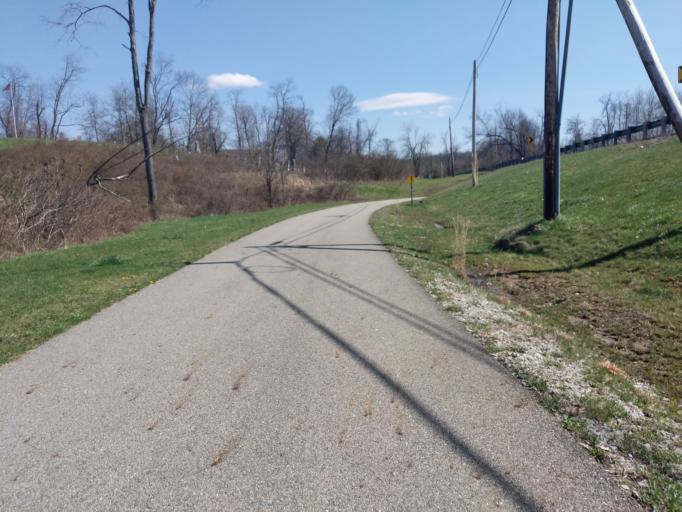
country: US
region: Ohio
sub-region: Athens County
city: The Plains
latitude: 39.3687
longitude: -82.1252
